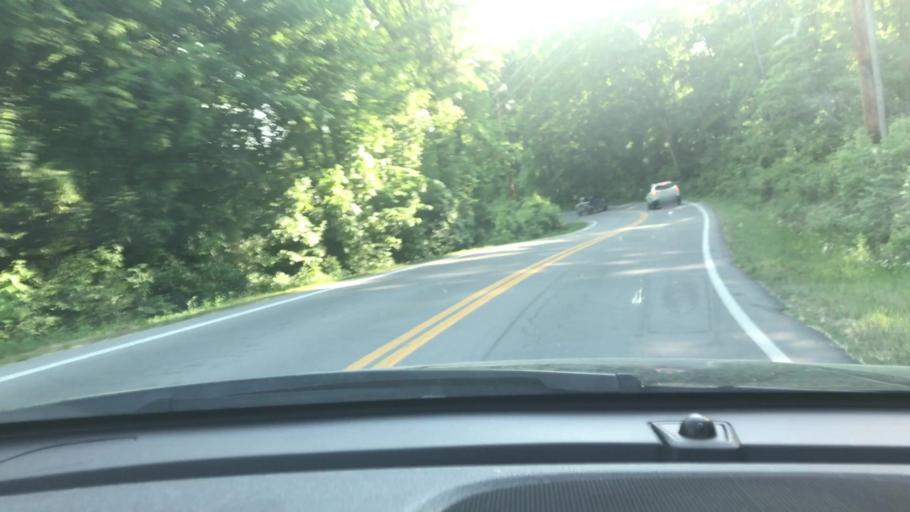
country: US
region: Tennessee
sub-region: Dickson County
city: Charlotte
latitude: 36.2041
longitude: -87.2861
